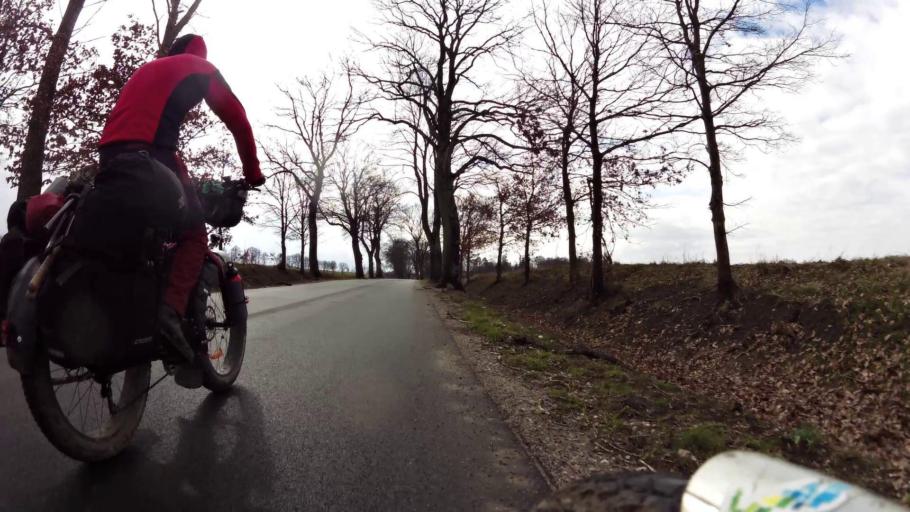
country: PL
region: Pomeranian Voivodeship
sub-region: Powiat bytowski
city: Kolczyglowy
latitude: 54.2236
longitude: 17.2405
